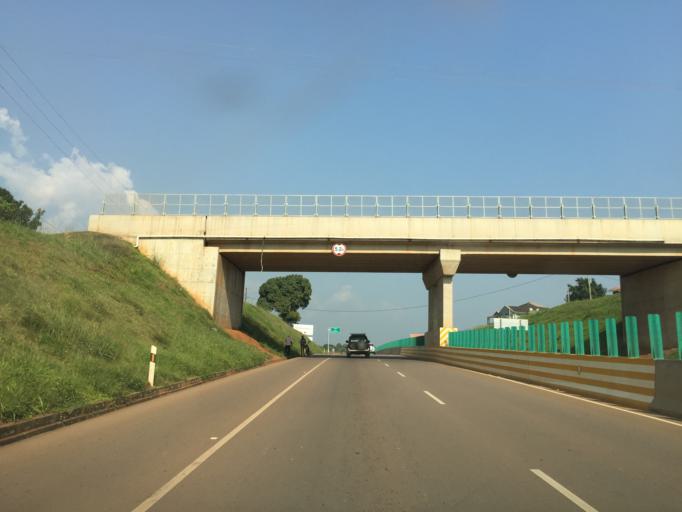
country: UG
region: Central Region
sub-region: Kampala District
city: Kampala
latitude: 0.2385
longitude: 32.6174
